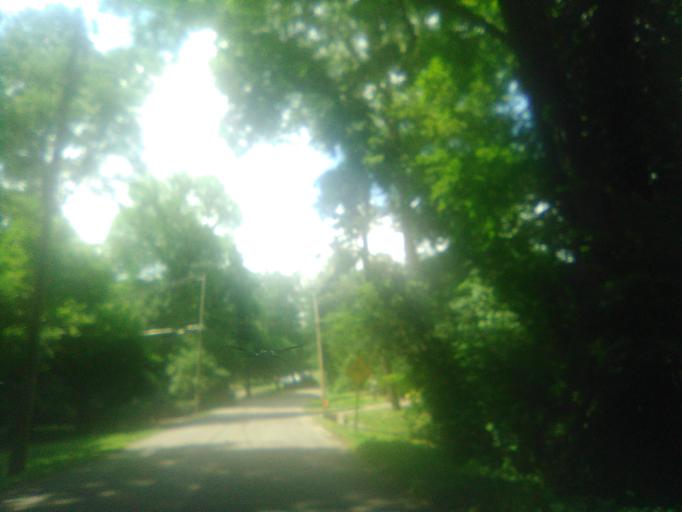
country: US
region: Tennessee
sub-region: Davidson County
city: Belle Meade
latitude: 36.1112
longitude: -86.8482
